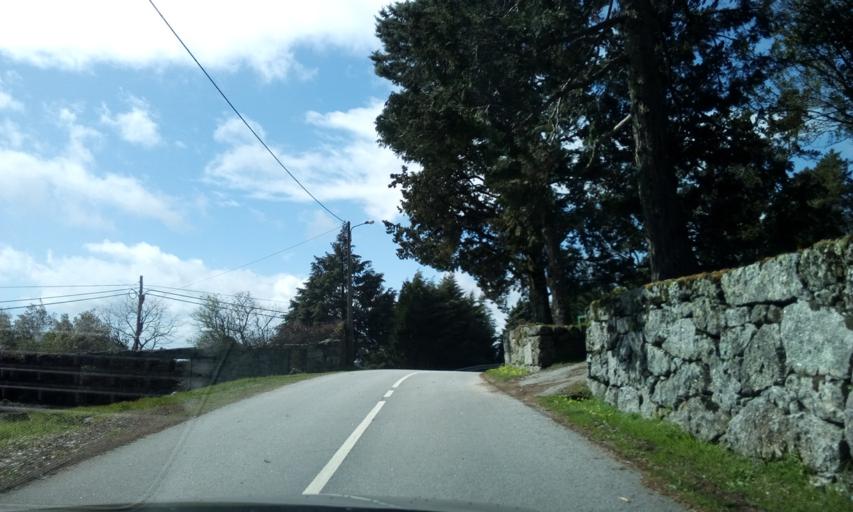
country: PT
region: Guarda
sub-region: Fornos de Algodres
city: Fornos de Algodres
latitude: 40.6323
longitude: -7.5448
